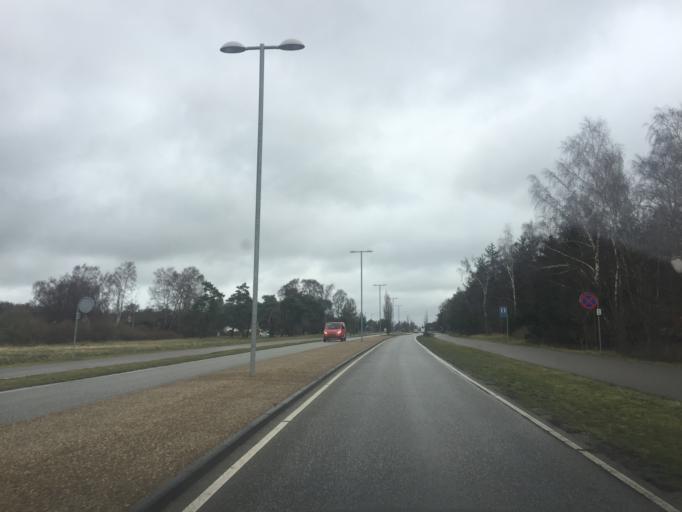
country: DK
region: Zealand
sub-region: Solrod Kommune
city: Solrod Strand
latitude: 55.5489
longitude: 12.2409
